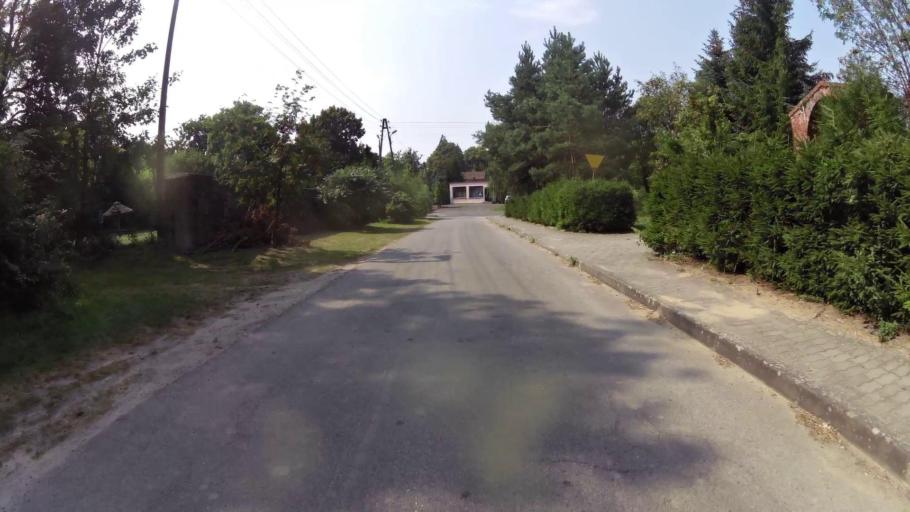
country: PL
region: West Pomeranian Voivodeship
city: Trzcinsko Zdroj
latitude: 52.9209
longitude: 14.5364
